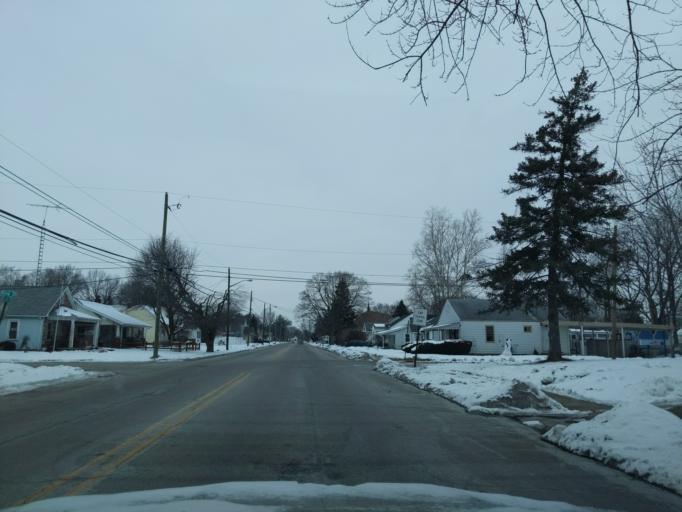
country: US
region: Indiana
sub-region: Tippecanoe County
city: Lafayette
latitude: 40.4043
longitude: -86.8767
